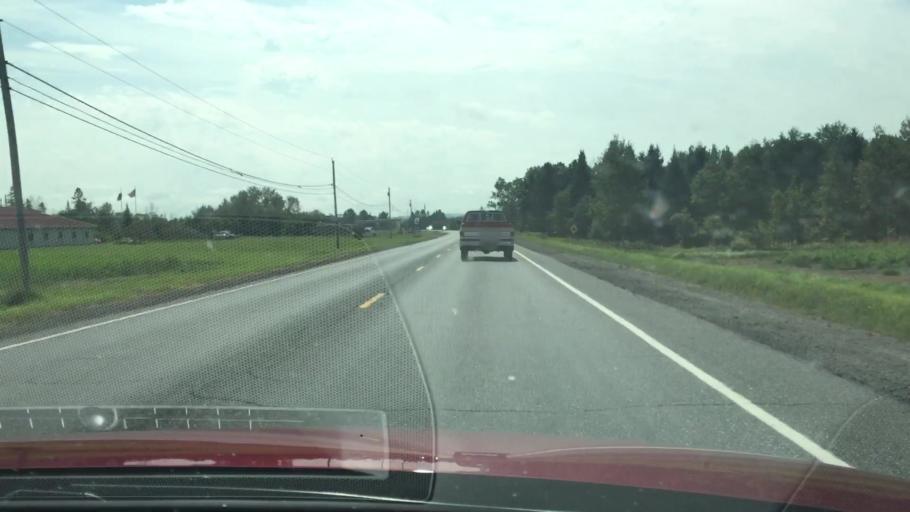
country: US
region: Maine
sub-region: Aroostook County
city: Presque Isle
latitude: 46.6145
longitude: -67.9807
